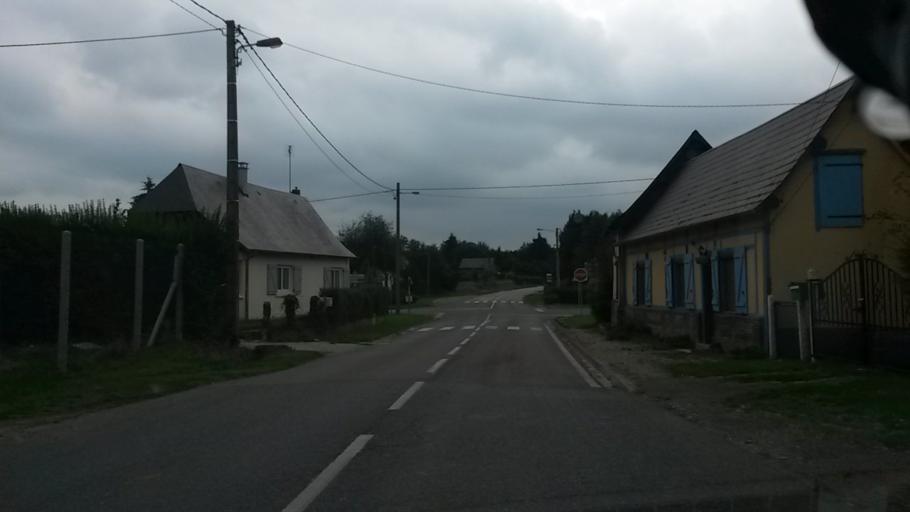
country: FR
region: Haute-Normandie
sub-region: Departement de la Seine-Maritime
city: Gaillefontaine
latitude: 49.6916
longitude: 1.6384
